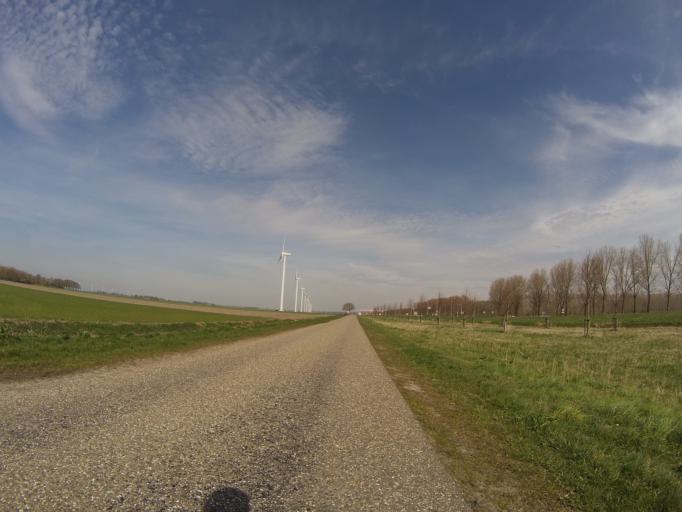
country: NL
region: Gelderland
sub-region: Gemeente Nijkerk
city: Nijkerk
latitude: 52.2790
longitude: 5.4623
